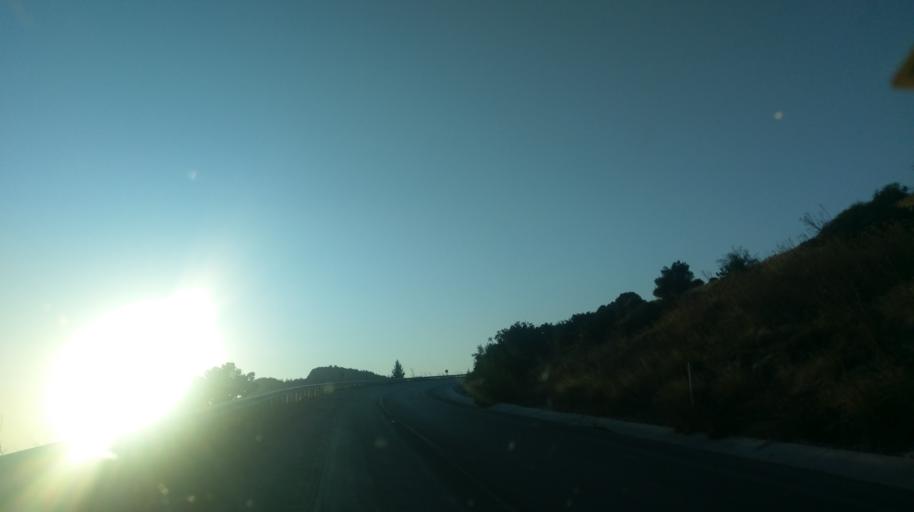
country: CY
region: Lefkosia
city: Nicosia
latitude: 35.2746
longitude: 33.4844
